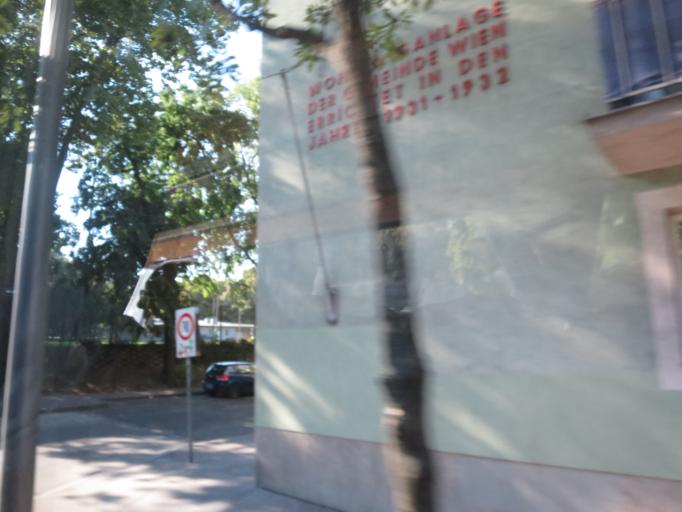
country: AT
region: Vienna
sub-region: Wien Stadt
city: Vienna
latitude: 48.1834
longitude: 16.3461
